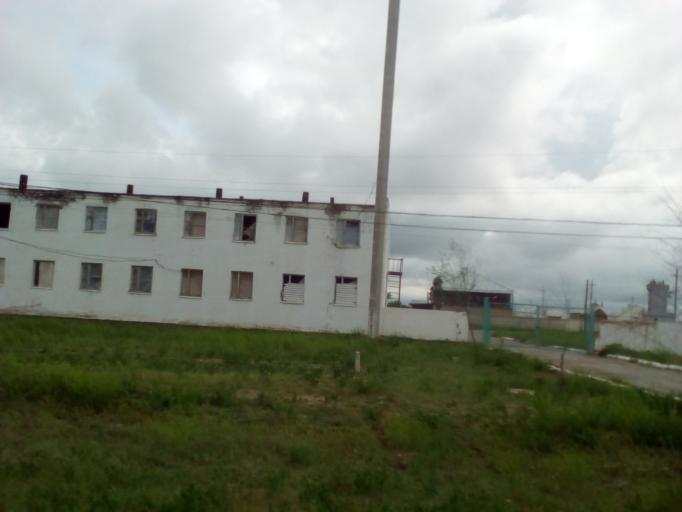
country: KZ
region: Ongtustik Qazaqstan
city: Sholaqqkorghan
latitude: 43.7512
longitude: 69.1953
